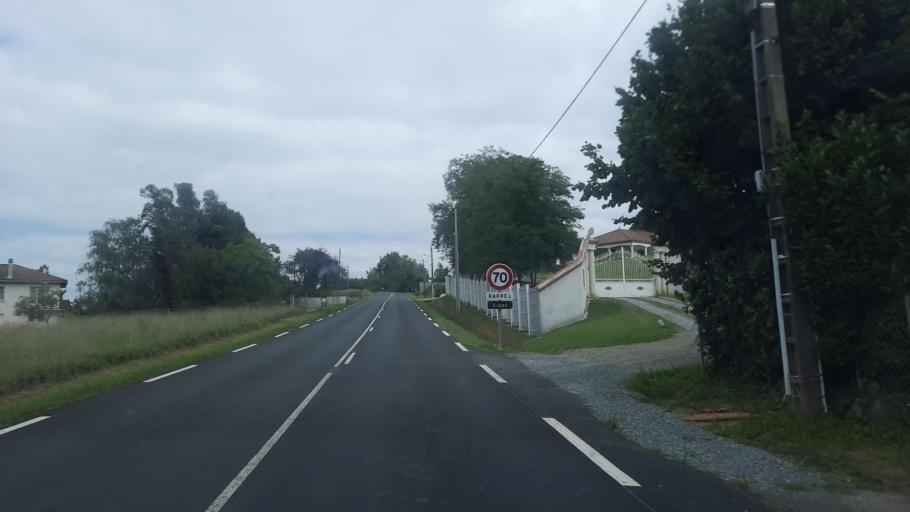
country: FR
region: Midi-Pyrenees
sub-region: Departement des Hautes-Pyrenees
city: Orleix
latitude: 43.2561
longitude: 0.1384
